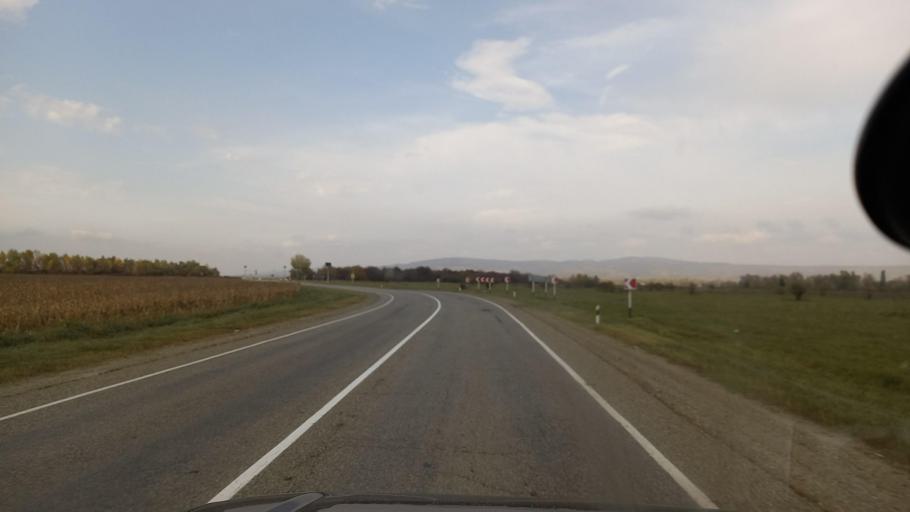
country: RU
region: Krasnodarskiy
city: Shedok
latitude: 44.2685
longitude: 40.8700
